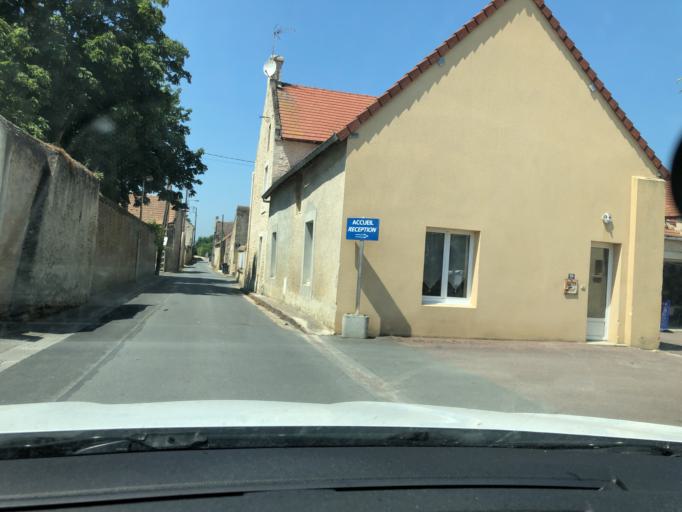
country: FR
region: Lower Normandy
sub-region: Departement du Calvados
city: Lion-sur-Mer
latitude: 49.3041
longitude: -0.3306
